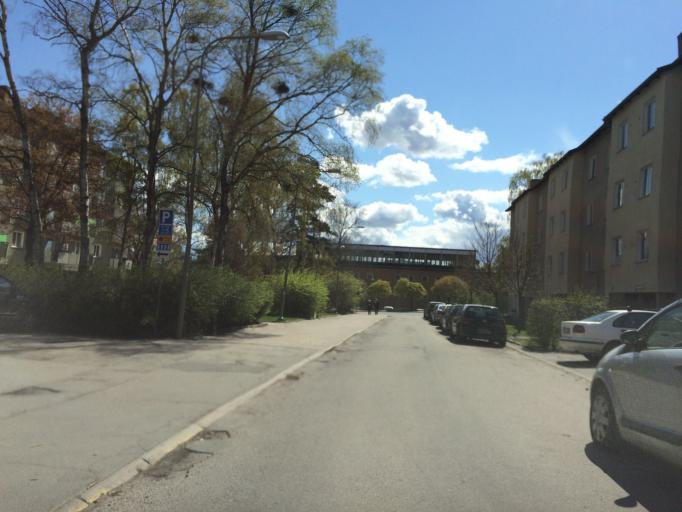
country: SE
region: Stockholm
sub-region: Huddinge Kommun
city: Segeltorp
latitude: 59.2942
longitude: 17.9760
